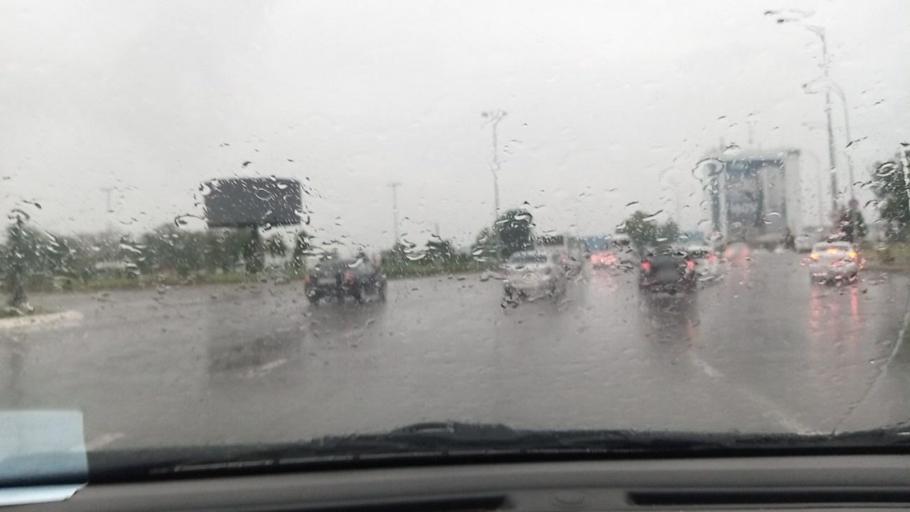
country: UZ
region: Toshkent Shahri
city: Bektemir
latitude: 41.2684
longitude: 69.3658
